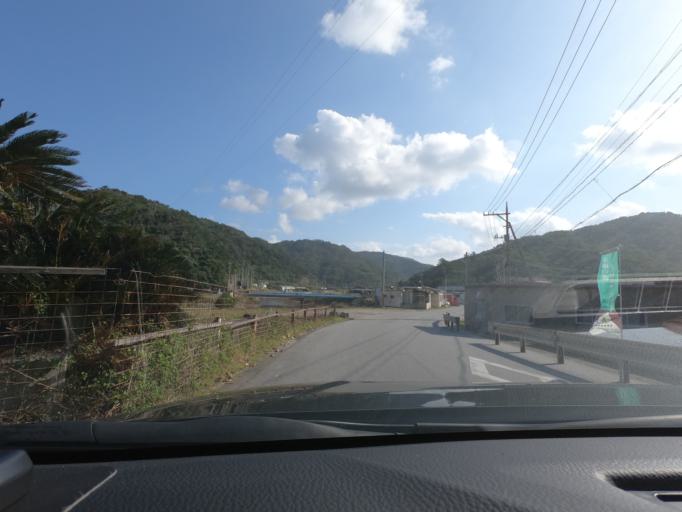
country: JP
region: Okinawa
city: Nago
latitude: 26.7657
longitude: 128.2036
